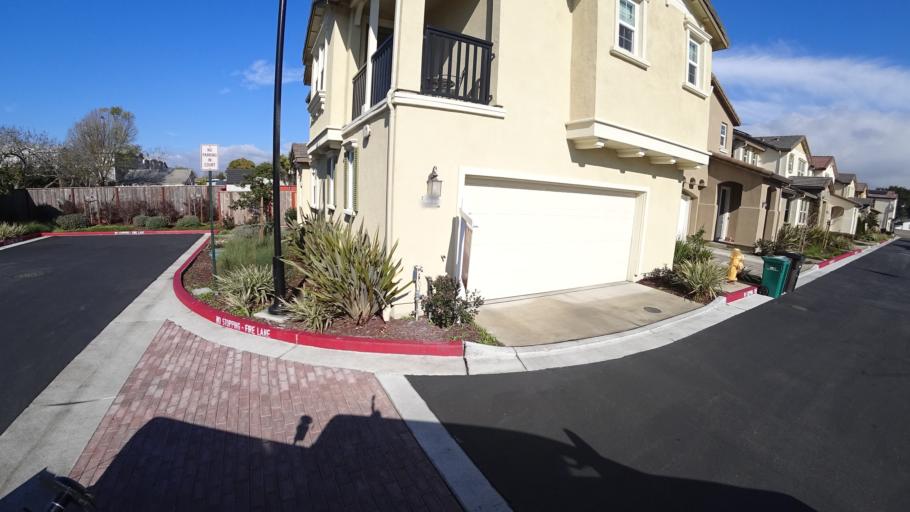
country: US
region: California
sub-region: Alameda County
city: San Lorenzo
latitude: 37.6503
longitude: -122.1168
